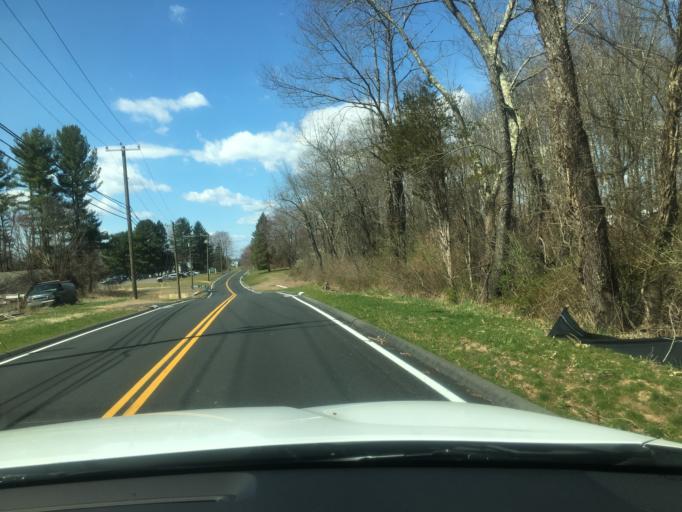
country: US
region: Connecticut
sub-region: Hartford County
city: Hazardville
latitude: 41.9585
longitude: -72.5295
